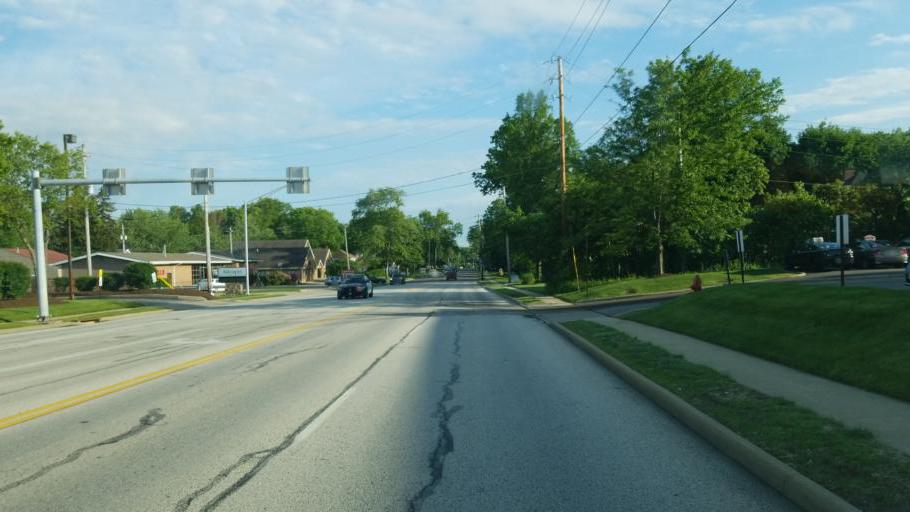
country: US
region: Ohio
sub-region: Summit County
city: Stow
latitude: 41.1657
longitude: -81.4405
